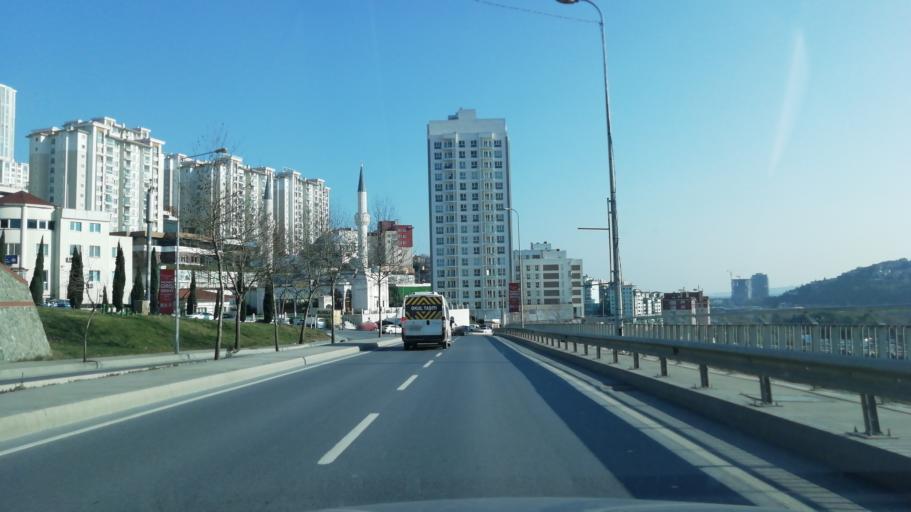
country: TR
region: Istanbul
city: Esenyurt
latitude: 41.0755
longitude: 28.6906
